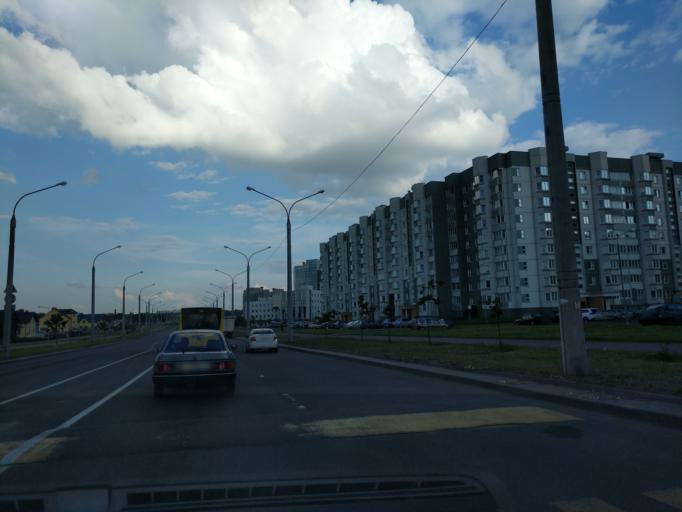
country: BY
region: Minsk
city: Zhdanovichy
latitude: 53.9336
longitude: 27.4371
